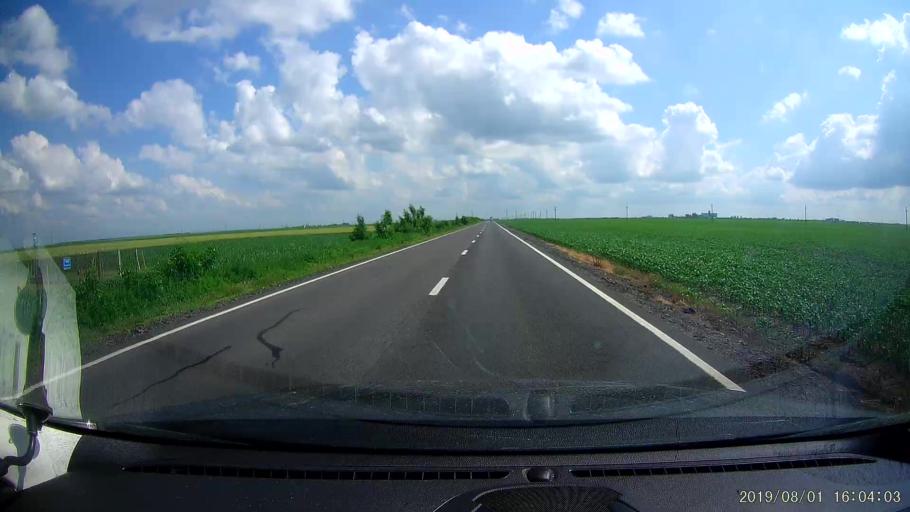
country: RO
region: Calarasi
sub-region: Comuna Dragalina
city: Drajna Noua
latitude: 44.4577
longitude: 27.3819
